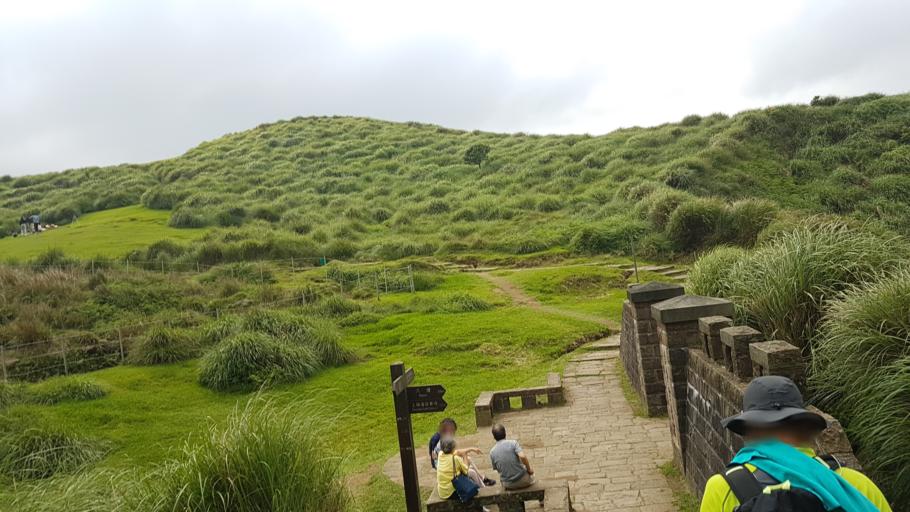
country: TW
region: Taipei
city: Taipei
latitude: 25.1663
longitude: 121.5780
